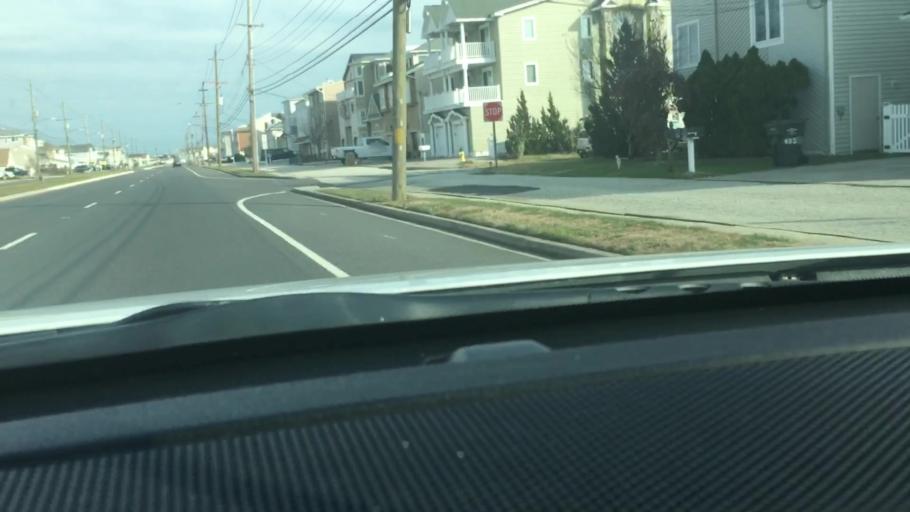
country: US
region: New Jersey
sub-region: Atlantic County
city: Atlantic City
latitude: 39.3912
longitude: -74.4100
